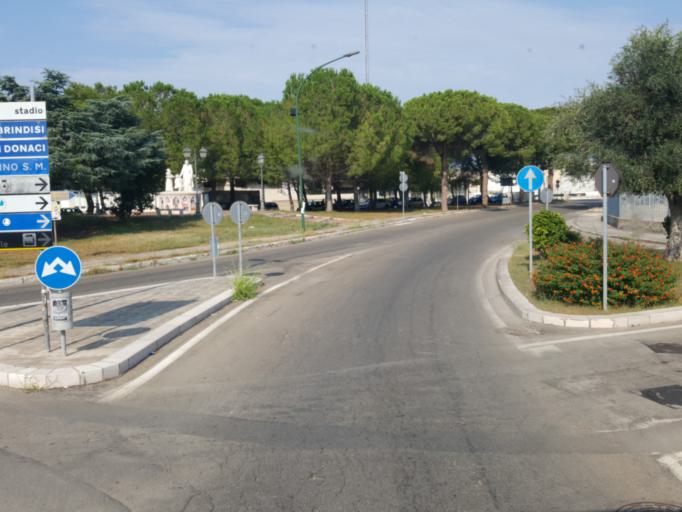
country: IT
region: Apulia
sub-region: Provincia di Lecce
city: Campi Salentina
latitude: 40.4033
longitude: 18.0162
